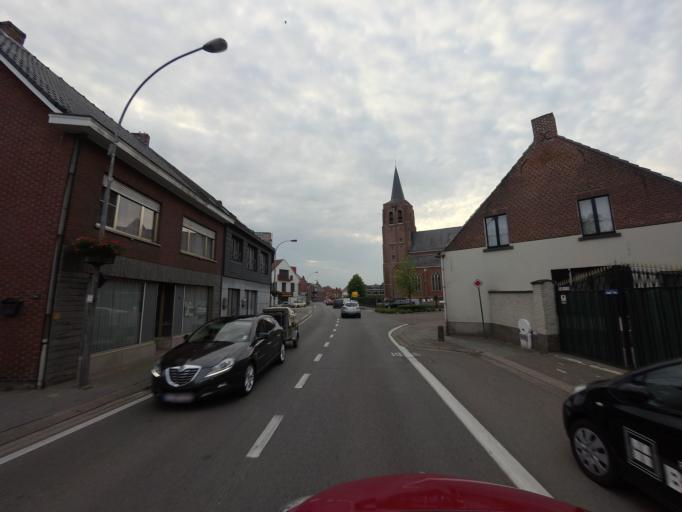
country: BE
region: Flanders
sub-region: Provincie Antwerpen
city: Lille
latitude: 51.2630
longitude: 4.7871
